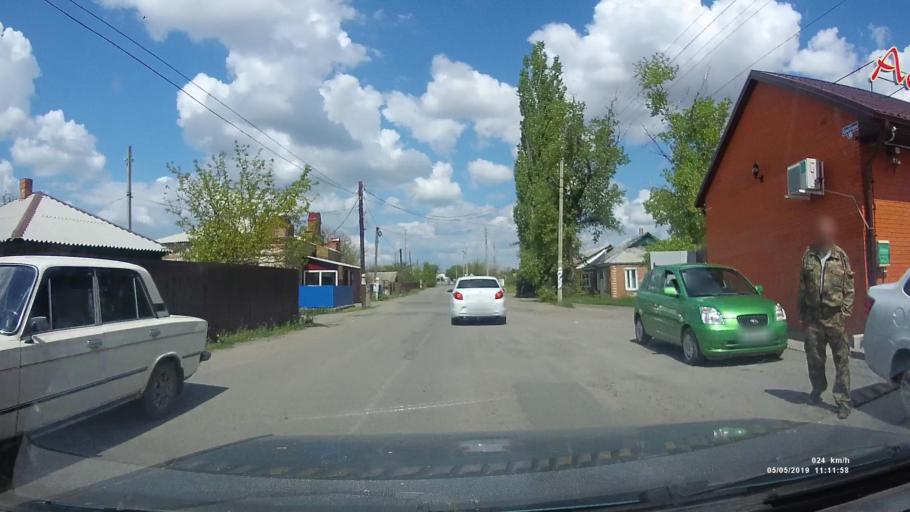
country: RU
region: Rostov
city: Ust'-Donetskiy
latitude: 47.7478
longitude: 40.9433
